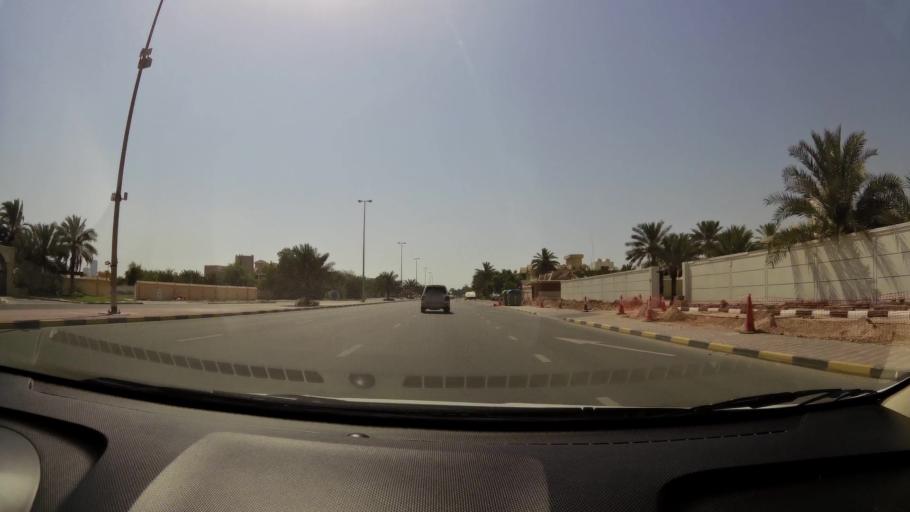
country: AE
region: Ajman
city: Ajman
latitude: 25.4044
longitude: 55.4754
